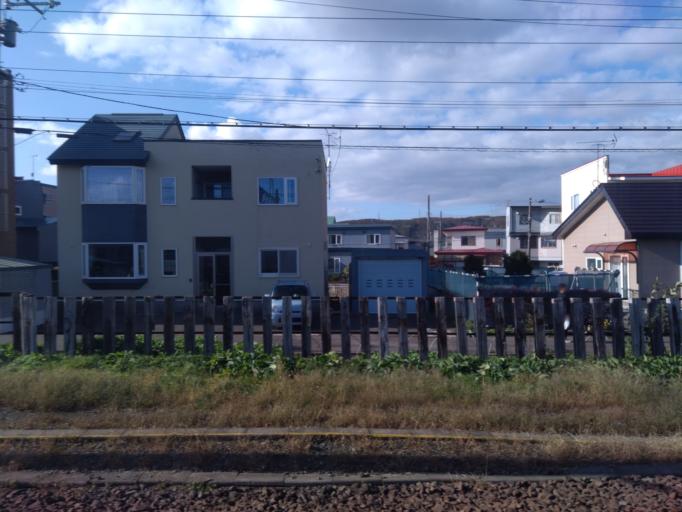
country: JP
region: Hokkaido
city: Muroran
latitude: 42.3525
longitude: 141.0307
